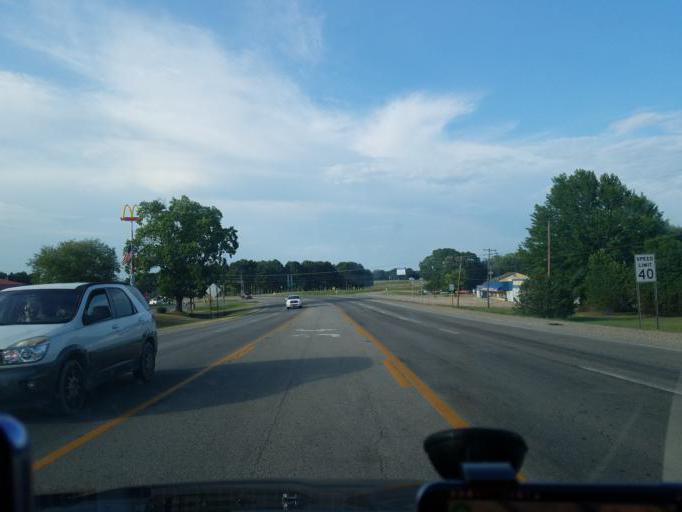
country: US
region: Arkansas
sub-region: White County
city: Bald Knob
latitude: 35.3167
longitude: -91.5627
